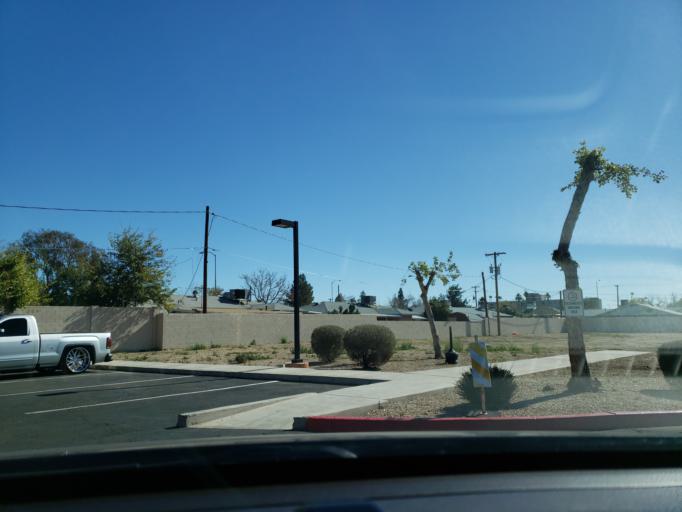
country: US
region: Arizona
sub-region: Maricopa County
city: Mesa
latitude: 33.4141
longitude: -111.8170
